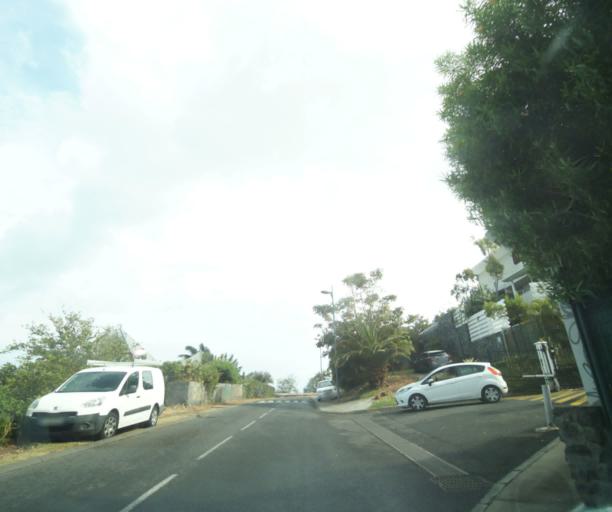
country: RE
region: Reunion
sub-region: Reunion
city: Saint-Paul
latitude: -21.0475
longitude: 55.2251
